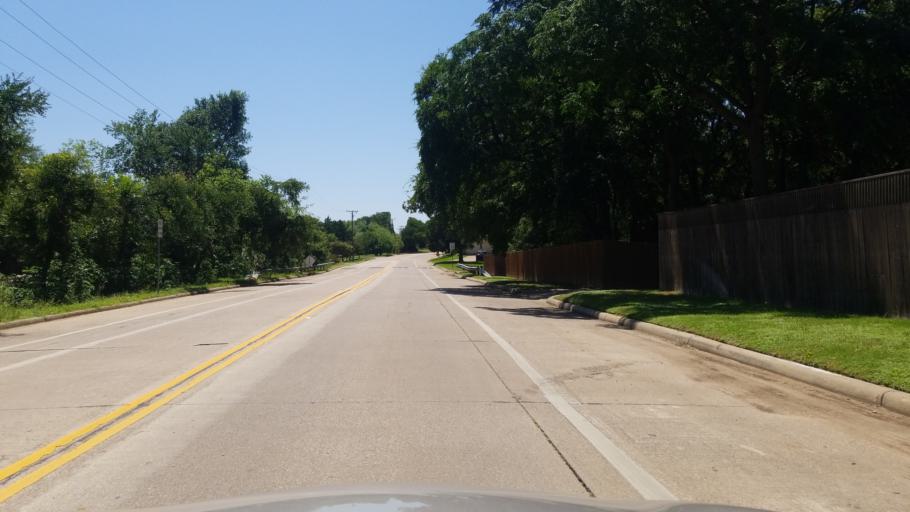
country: US
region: Texas
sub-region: Dallas County
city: Grand Prairie
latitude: 32.6787
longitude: -97.0009
